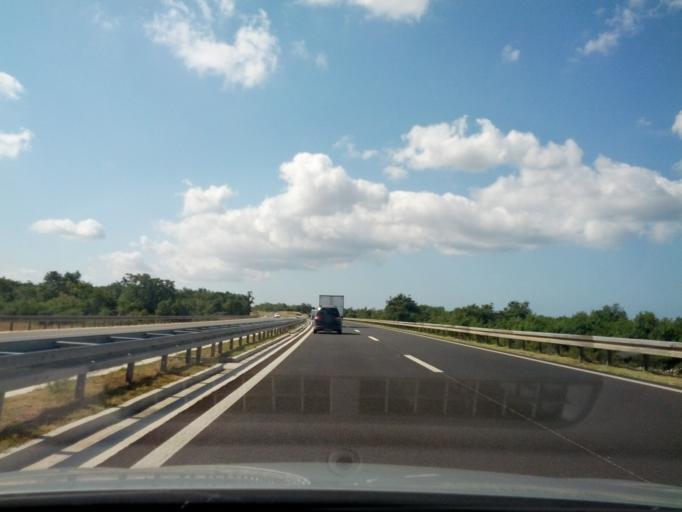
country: HR
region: Istarska
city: Vodnjan
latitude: 45.0062
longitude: 13.8373
